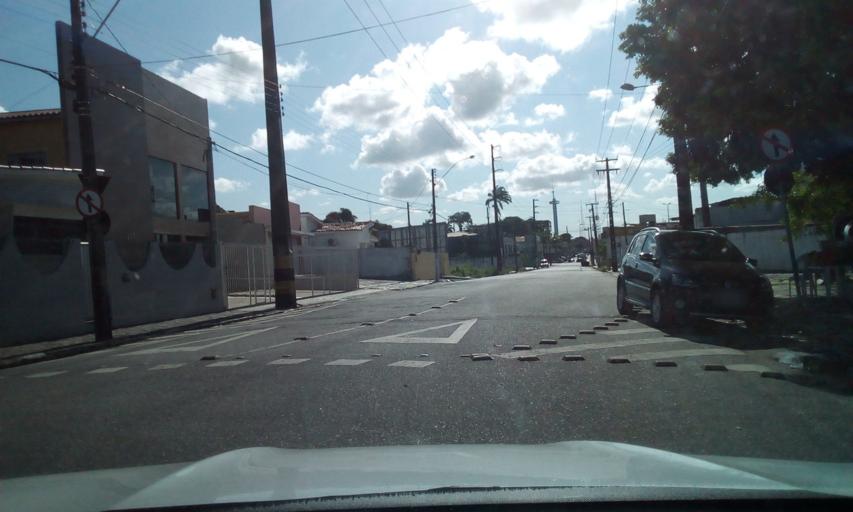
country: BR
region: Paraiba
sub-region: Joao Pessoa
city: Joao Pessoa
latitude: -7.1208
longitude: -34.8659
